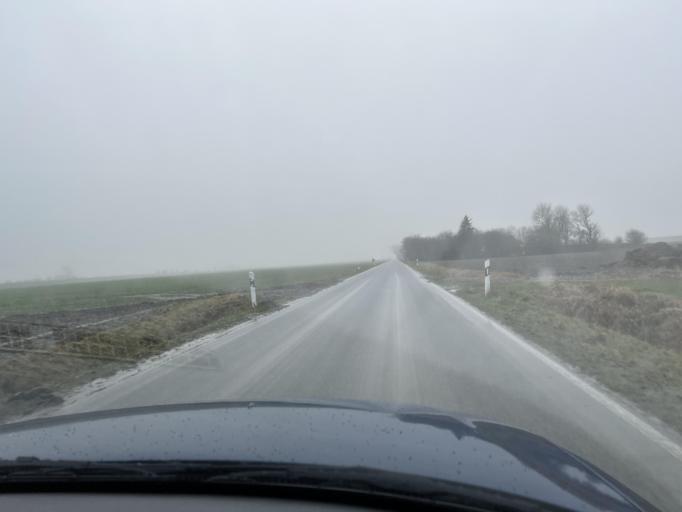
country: DE
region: Schleswig-Holstein
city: Schulp
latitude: 54.2611
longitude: 8.9202
